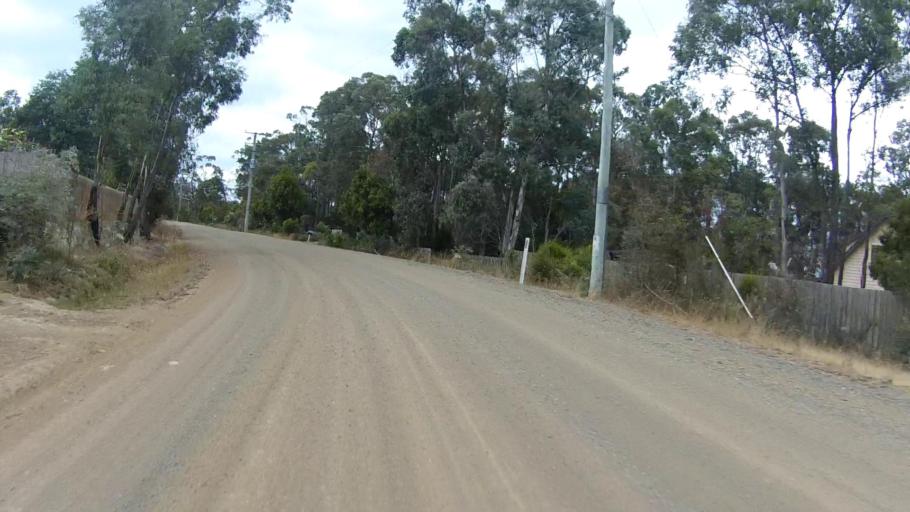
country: AU
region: Tasmania
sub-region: Huon Valley
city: Cygnet
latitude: -43.2295
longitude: 147.0972
